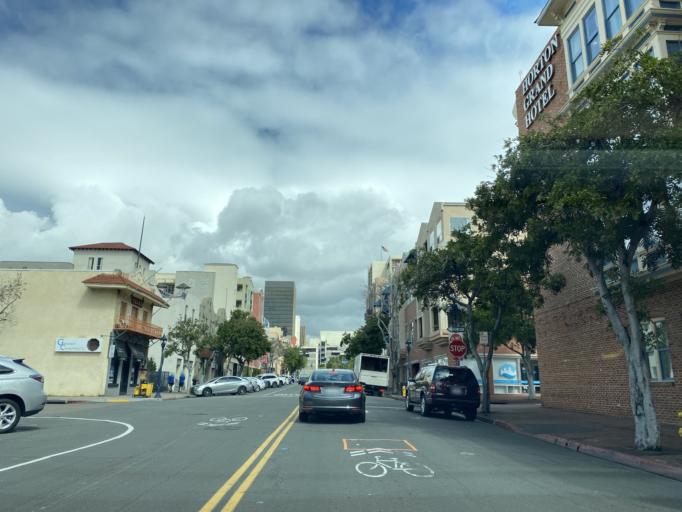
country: US
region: California
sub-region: San Diego County
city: San Diego
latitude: 32.7101
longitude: -117.1618
